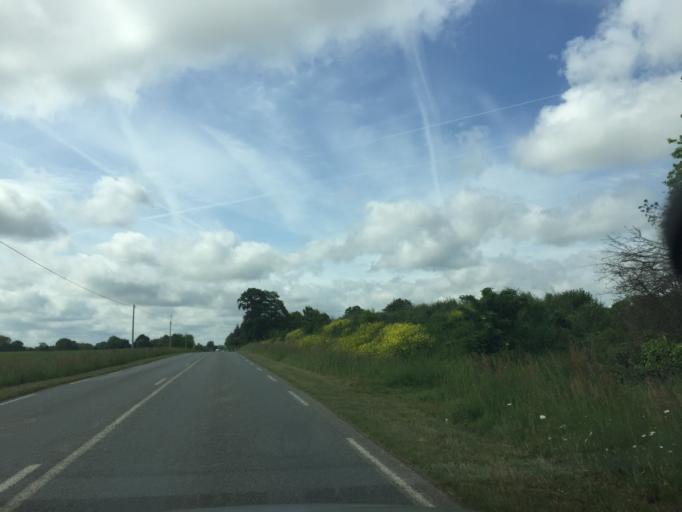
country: FR
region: Brittany
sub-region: Departement des Cotes-d'Armor
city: Crehen
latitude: 48.5574
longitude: -2.1919
